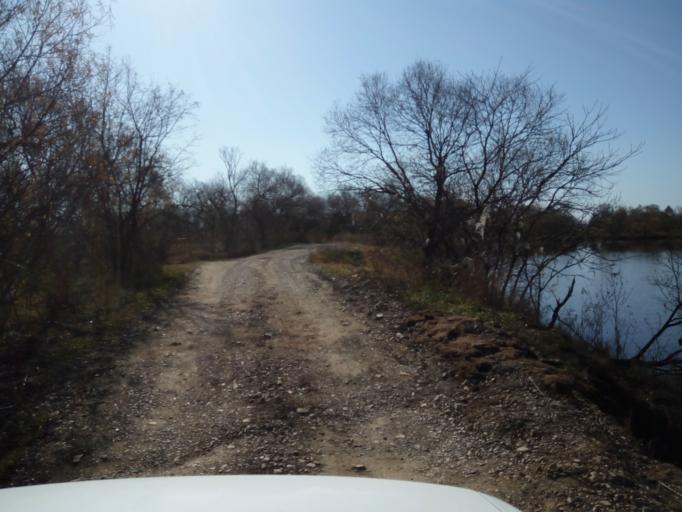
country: RU
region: Primorskiy
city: Dal'nerechensk
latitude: 45.9184
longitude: 133.7883
